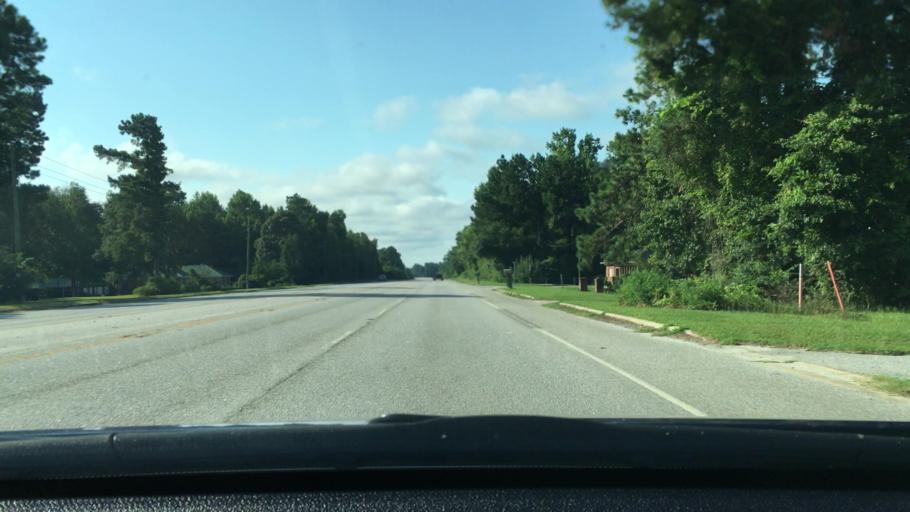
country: US
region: South Carolina
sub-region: Clarendon County
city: Manning
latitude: 33.7583
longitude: -80.2268
